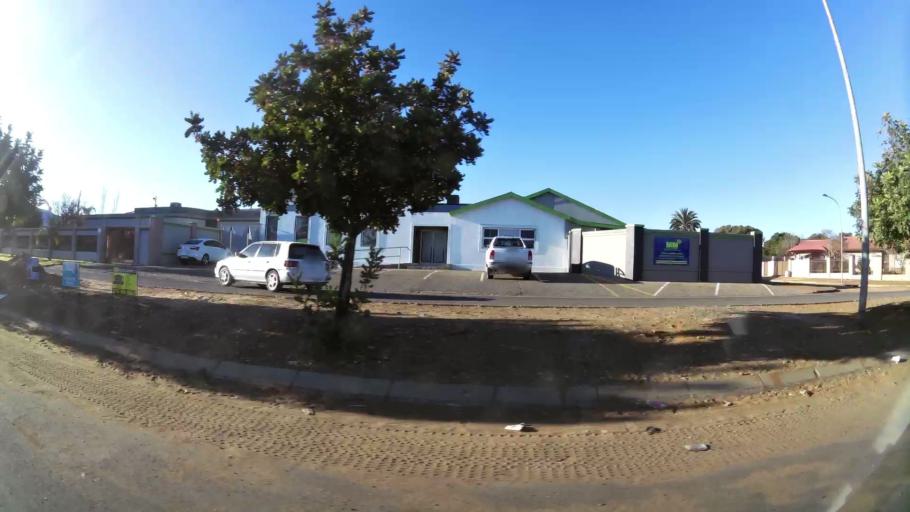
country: ZA
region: Northern Cape
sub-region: Frances Baard District Municipality
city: Kimberley
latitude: -28.7487
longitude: 24.7411
